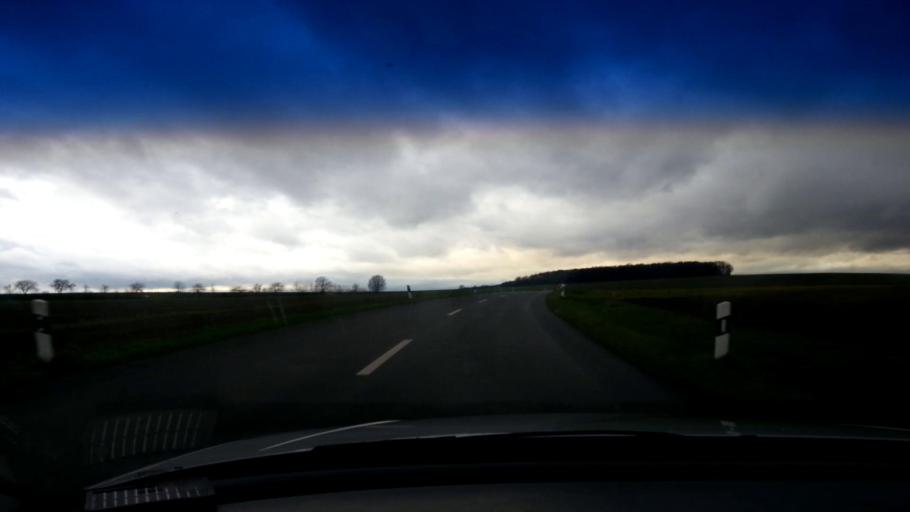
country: DE
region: Bavaria
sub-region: Upper Franconia
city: Ebensfeld
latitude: 50.0339
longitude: 10.9958
